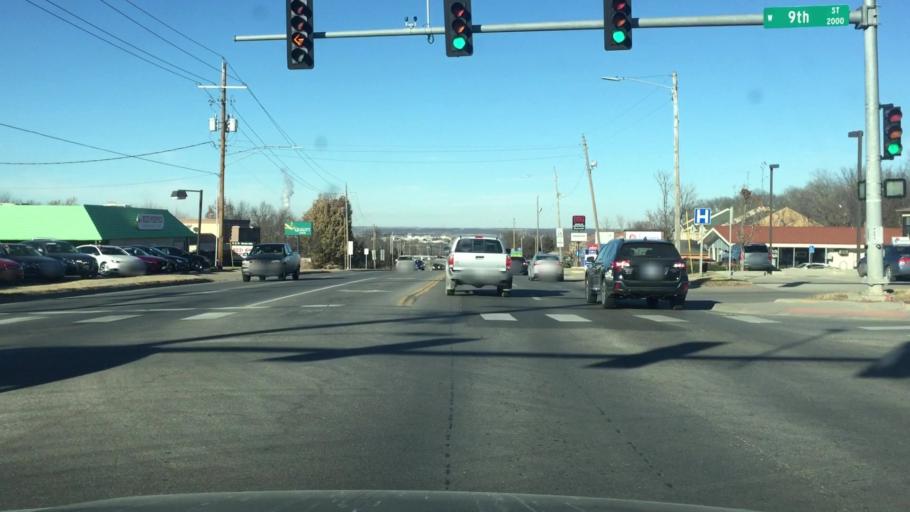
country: US
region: Kansas
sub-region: Douglas County
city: Lawrence
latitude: 38.9679
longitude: -95.2604
